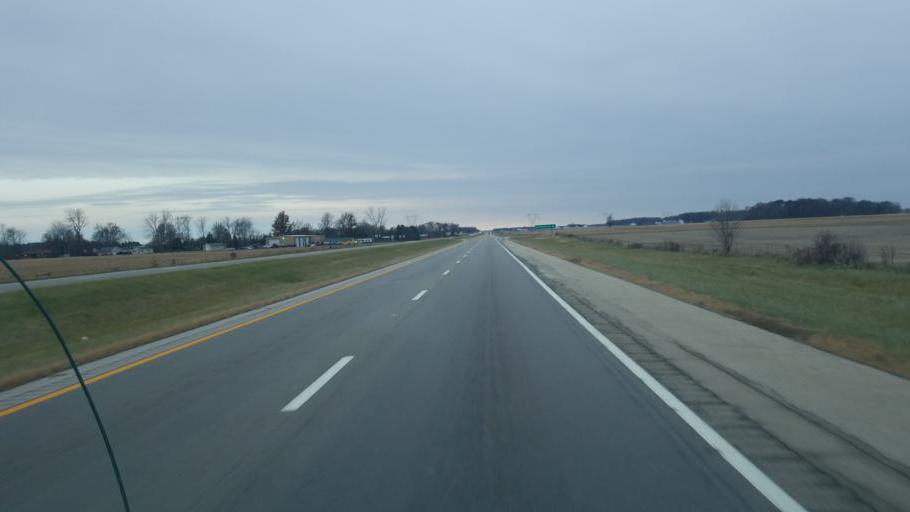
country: US
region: Ohio
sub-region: Auglaize County
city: Wapakoneta
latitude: 40.5650
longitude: -84.2562
